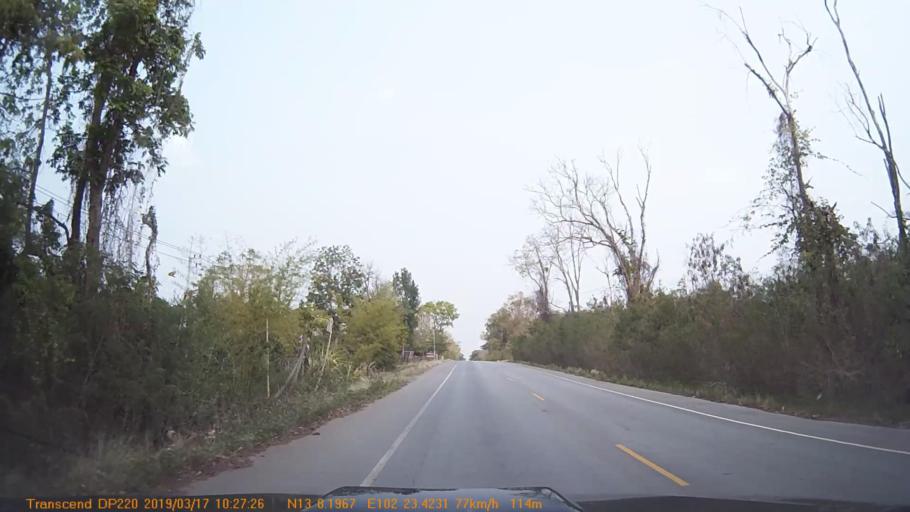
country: TH
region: Chanthaburi
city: Soi Dao
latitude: 13.1369
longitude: 102.3902
